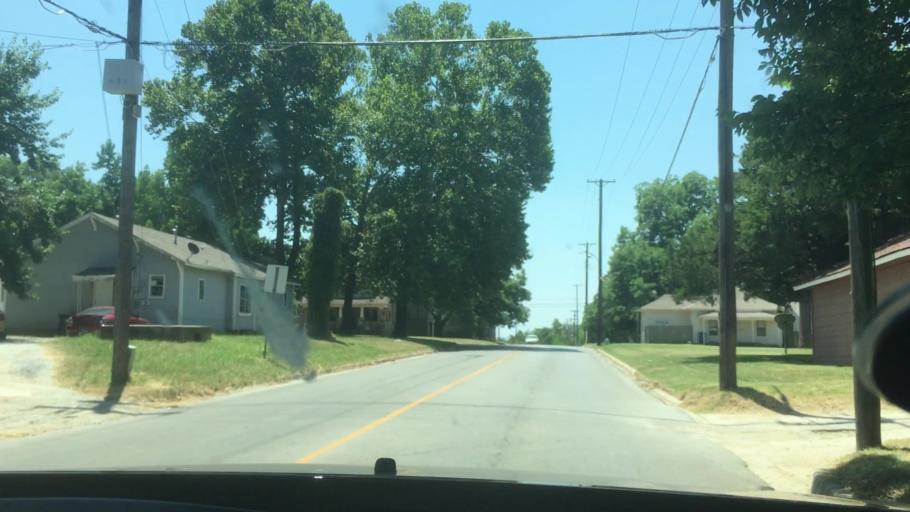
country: US
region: Oklahoma
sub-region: Pontotoc County
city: Ada
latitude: 34.7784
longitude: -96.6634
